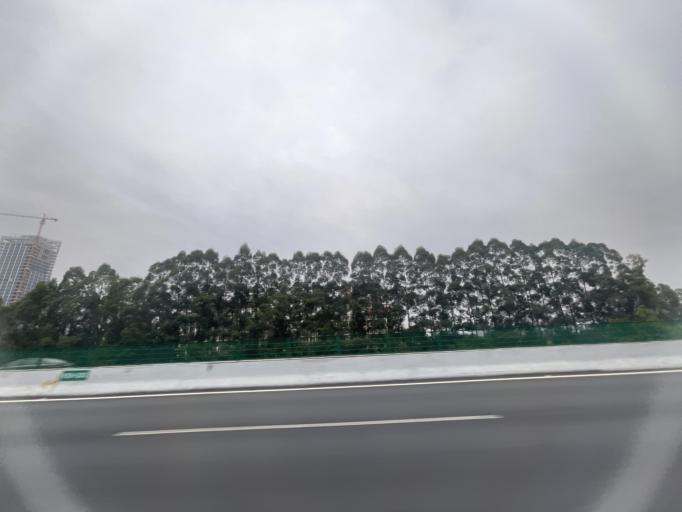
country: CN
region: Guangdong
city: Huangge
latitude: 22.7891
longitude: 113.5179
